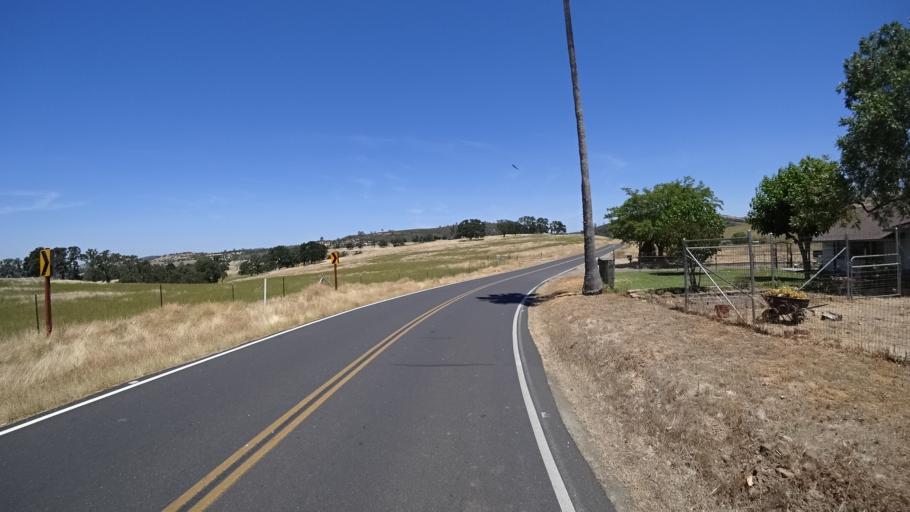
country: US
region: California
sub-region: Calaveras County
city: Valley Springs
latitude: 38.2285
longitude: -120.8191
